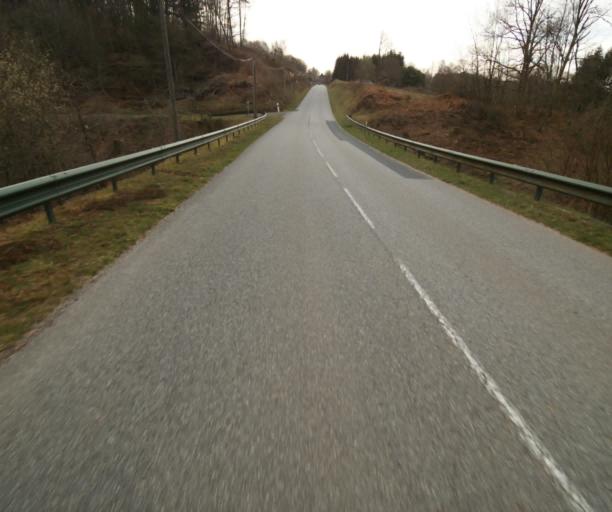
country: FR
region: Limousin
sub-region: Departement de la Correze
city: Correze
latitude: 45.4321
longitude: 1.8247
